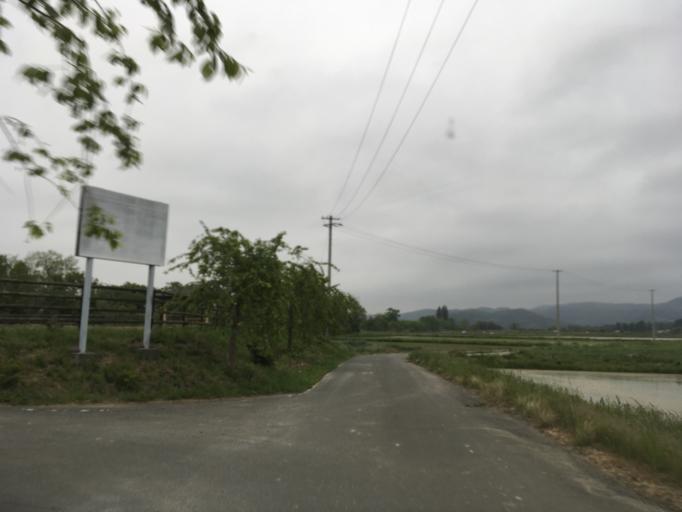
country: JP
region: Miyagi
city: Wakuya
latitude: 38.7099
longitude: 141.2842
